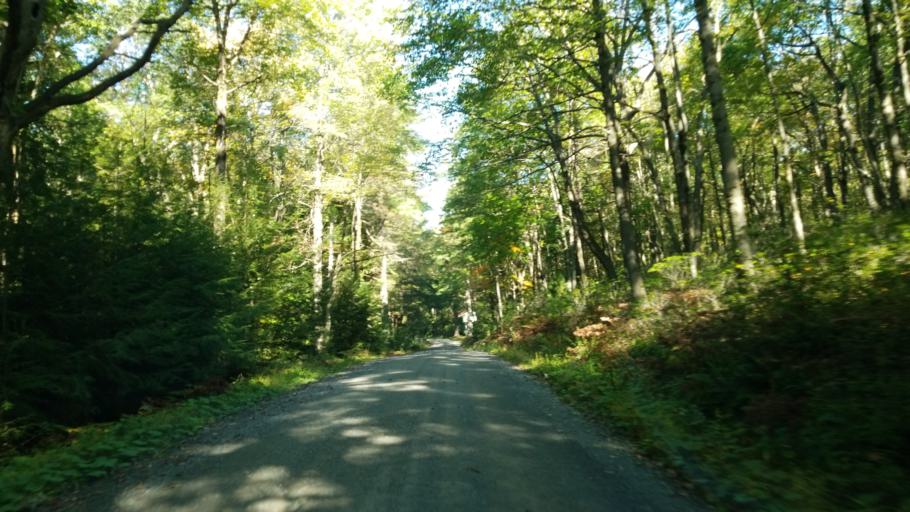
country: US
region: Pennsylvania
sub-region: Clearfield County
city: Hyde
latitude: 41.0874
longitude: -78.5338
